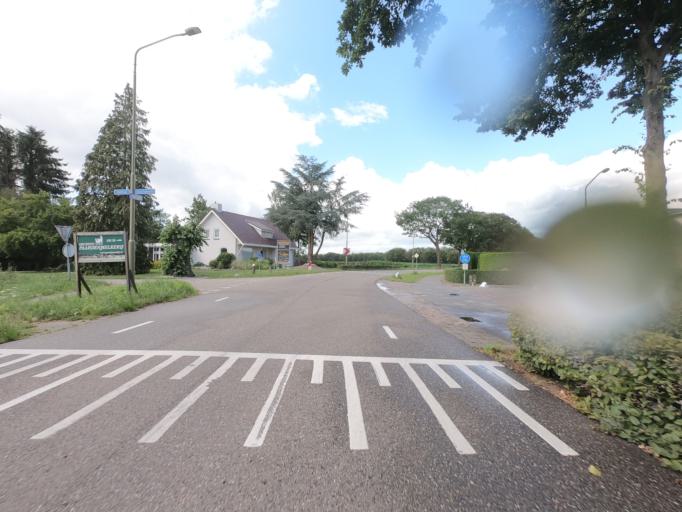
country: NL
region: North Brabant
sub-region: Gemeente Landerd
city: Zeeland
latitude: 51.7185
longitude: 5.6842
